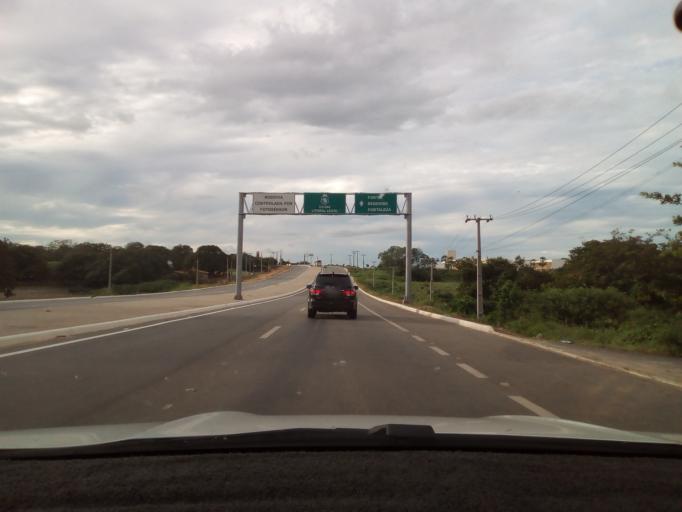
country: BR
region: Ceara
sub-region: Aracati
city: Aracati
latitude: -4.5705
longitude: -37.7917
